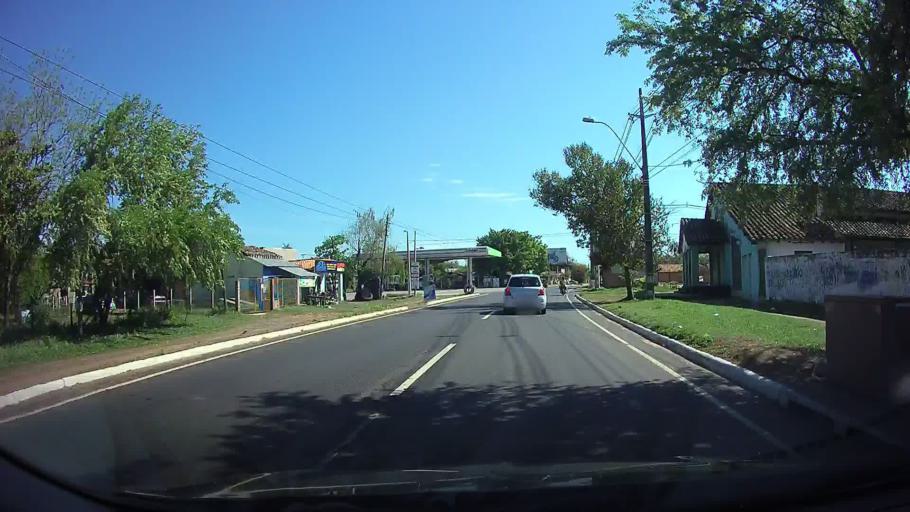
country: PY
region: Central
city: Ypacarai
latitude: -25.3979
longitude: -57.2829
